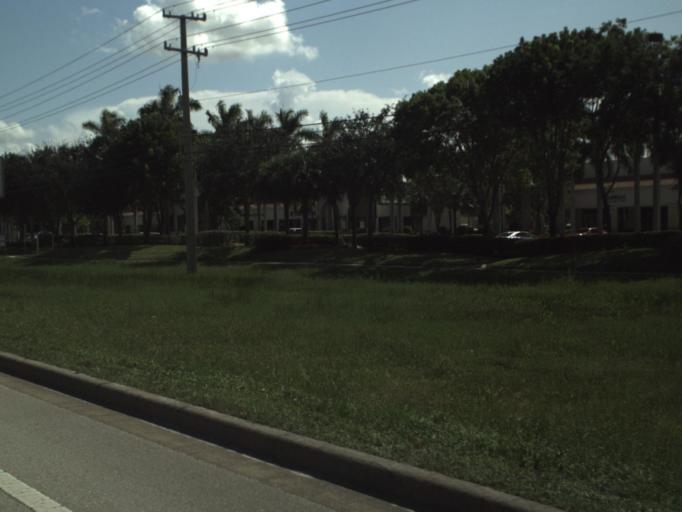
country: US
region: Florida
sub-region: Palm Beach County
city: Wellington
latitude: 26.6461
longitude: -80.2038
